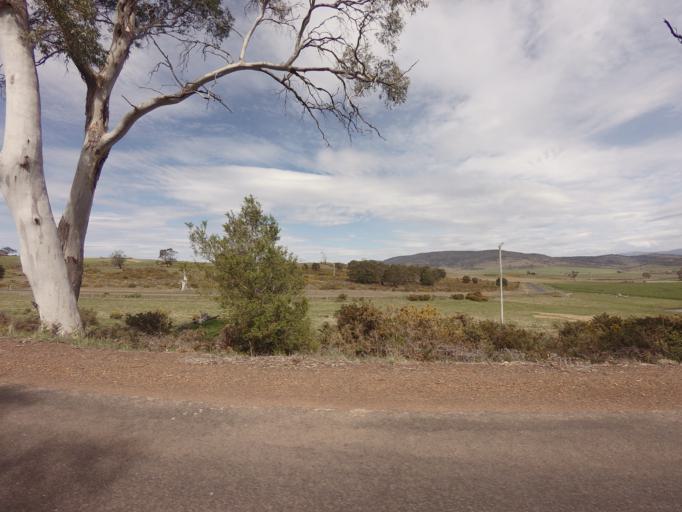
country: AU
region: Tasmania
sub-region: Northern Midlands
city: Evandale
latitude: -41.8951
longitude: 147.4082
